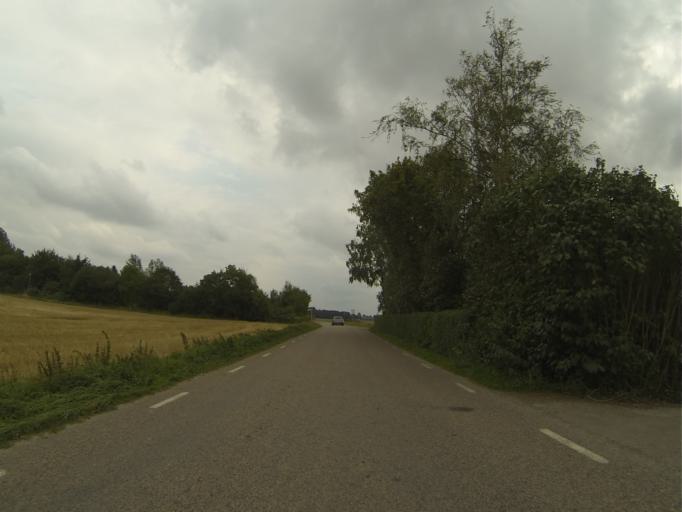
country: SE
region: Skane
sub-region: Lunds Kommun
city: Lund
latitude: 55.7777
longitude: 13.2121
